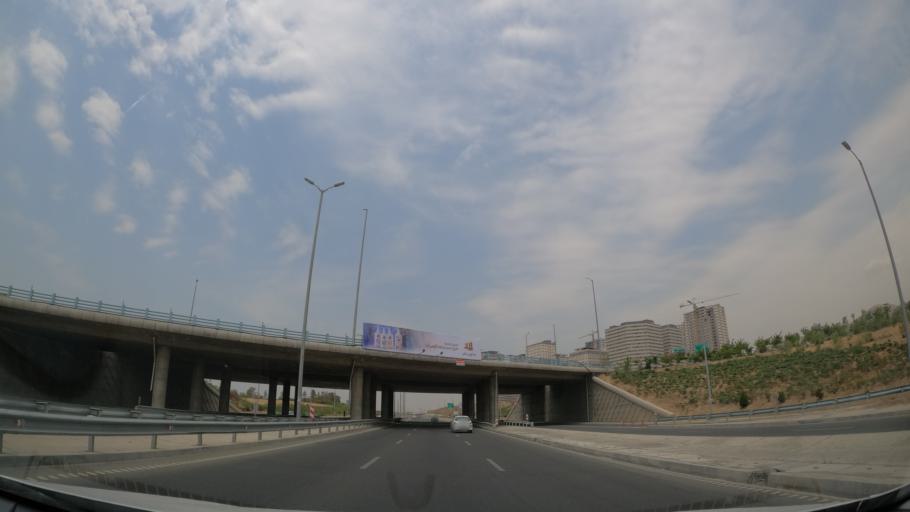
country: IR
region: Tehran
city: Shahr-e Qods
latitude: 35.7458
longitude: 51.1911
